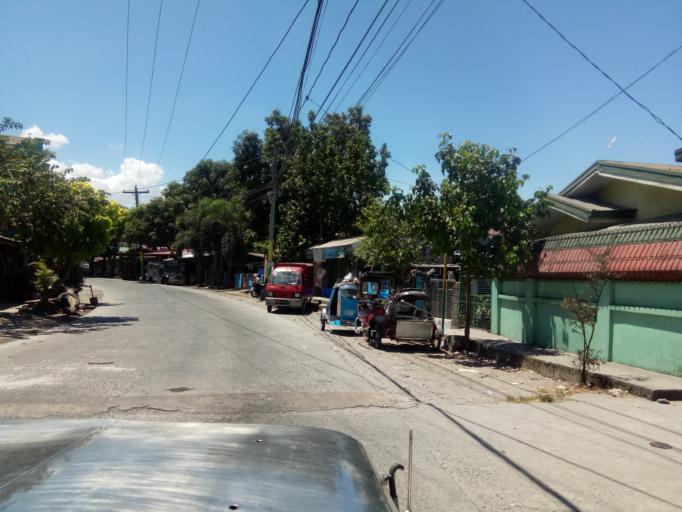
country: PH
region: Calabarzon
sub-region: Province of Cavite
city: Dasmarinas
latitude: 14.3236
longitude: 120.9704
